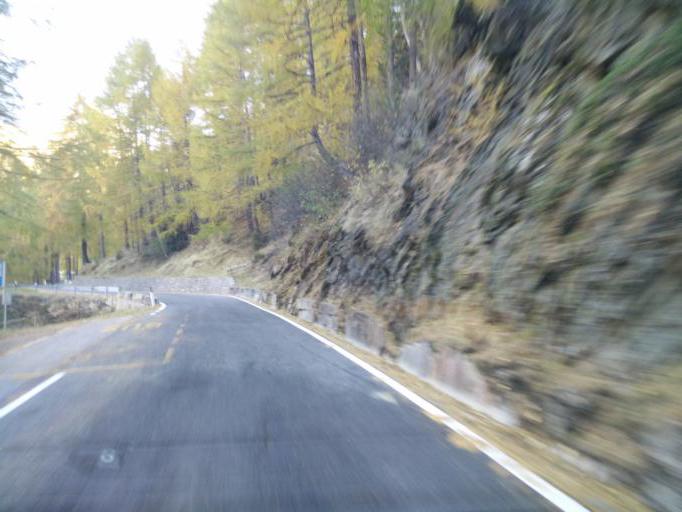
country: IT
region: Trentino-Alto Adige
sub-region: Bolzano
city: Moso in Passiria
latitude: 46.8715
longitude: 11.1620
